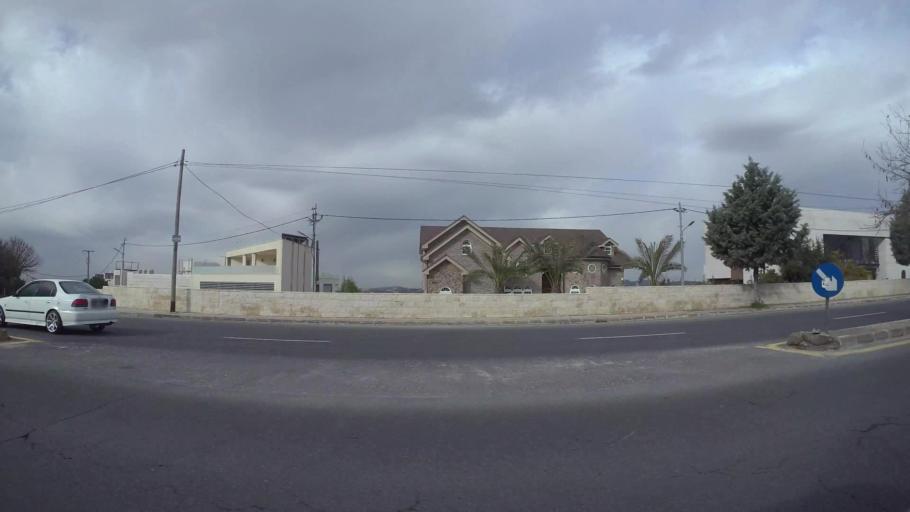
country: JO
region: Amman
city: Wadi as Sir
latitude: 31.9830
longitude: 35.8214
